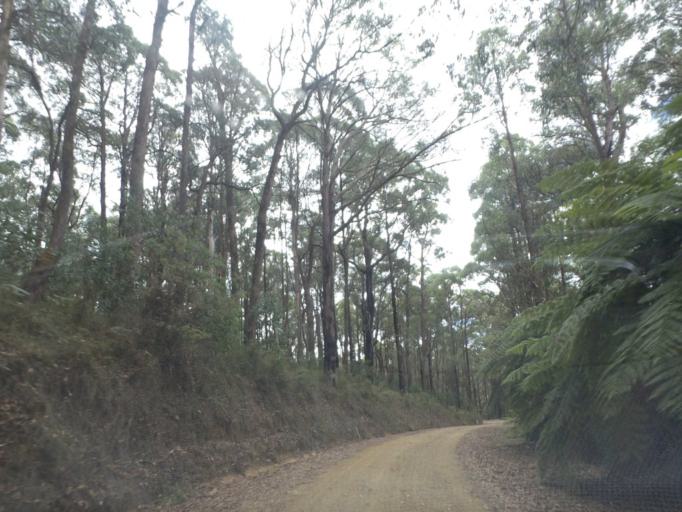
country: AU
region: Victoria
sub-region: Murrindindi
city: Alexandra
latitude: -37.4535
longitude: 145.9668
